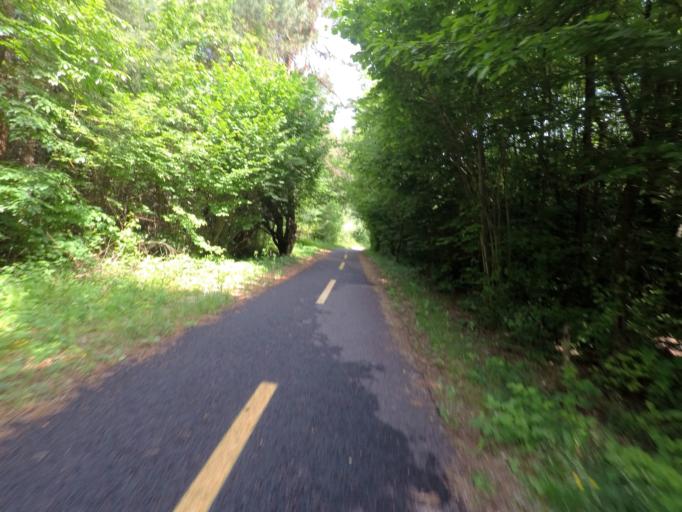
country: IT
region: Friuli Venezia Giulia
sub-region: Provincia di Udine
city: Cavazzo Carnico
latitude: 46.3780
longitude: 13.0327
